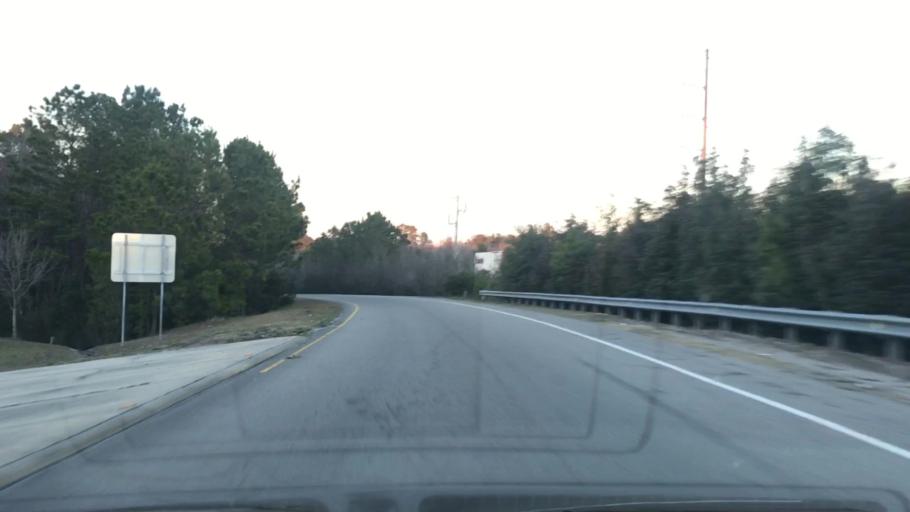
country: US
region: North Carolina
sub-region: Brunswick County
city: Shallotte
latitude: 33.9760
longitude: -78.4025
